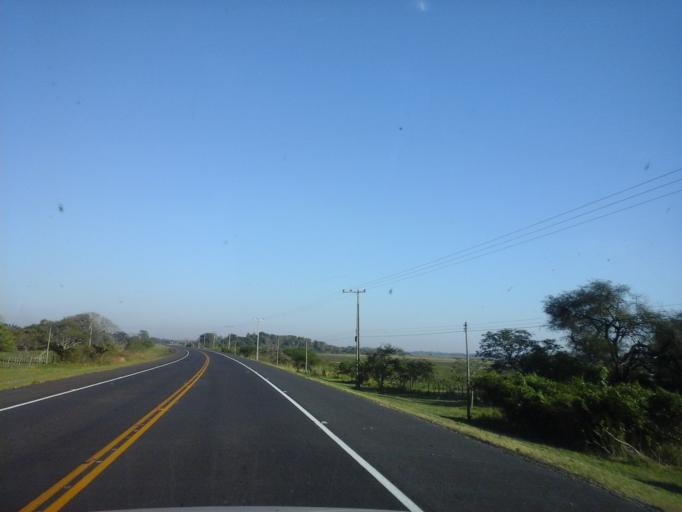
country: PY
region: Neembucu
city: Pilar
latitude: -26.8688
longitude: -58.1160
